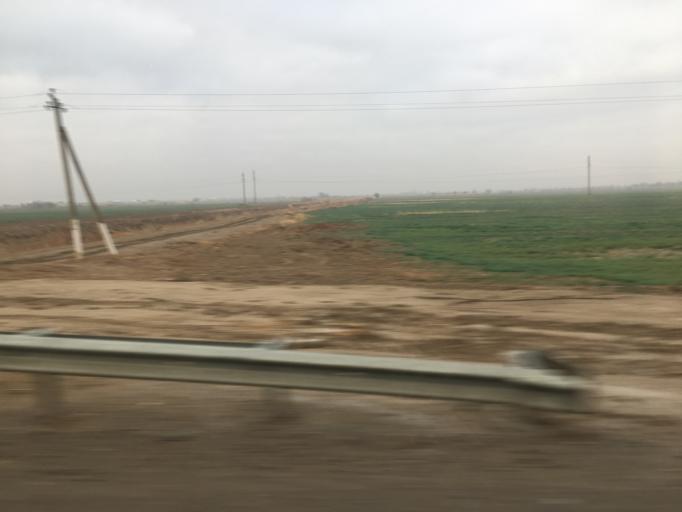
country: TM
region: Mary
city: Yoloeten
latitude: 37.2996
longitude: 62.3294
